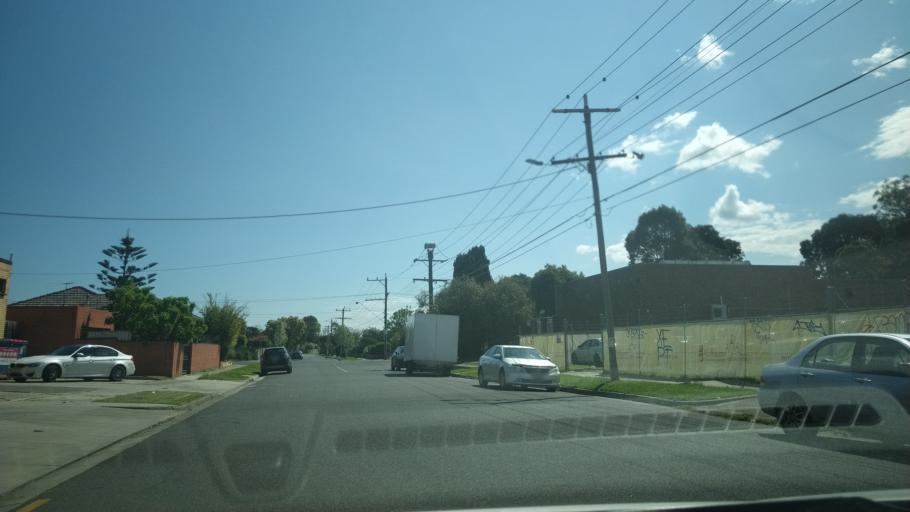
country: AU
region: Victoria
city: Highett
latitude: -37.9431
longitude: 145.0531
